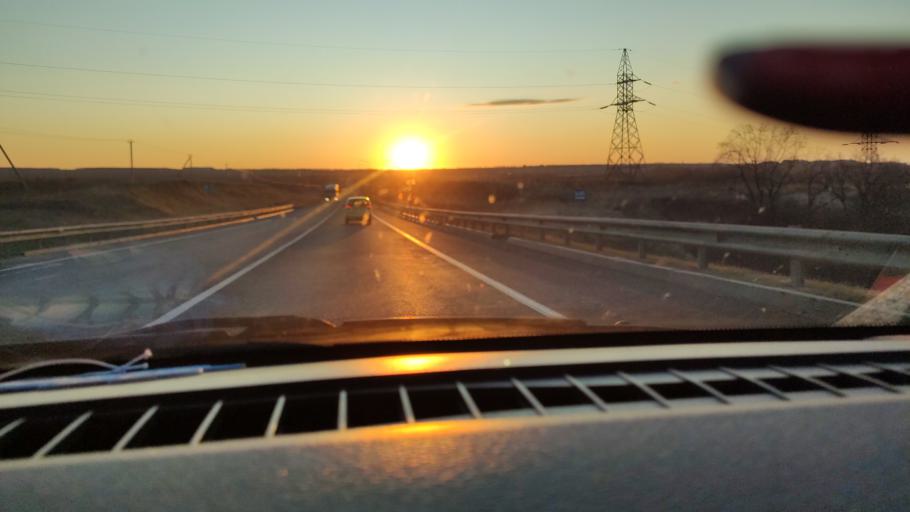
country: RU
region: Saratov
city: Yelshanka
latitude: 51.8233
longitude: 46.3802
